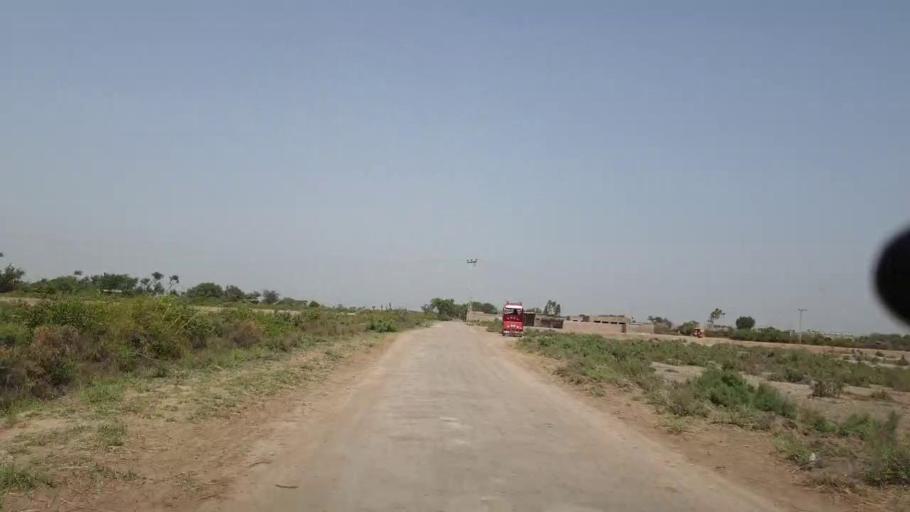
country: PK
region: Sindh
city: Matli
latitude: 25.0785
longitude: 68.6894
